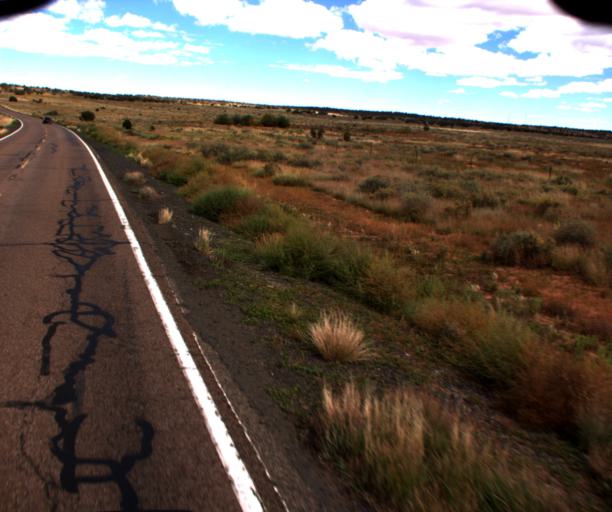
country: US
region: Arizona
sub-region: Navajo County
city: Heber-Overgaard
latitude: 34.6290
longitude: -110.3630
